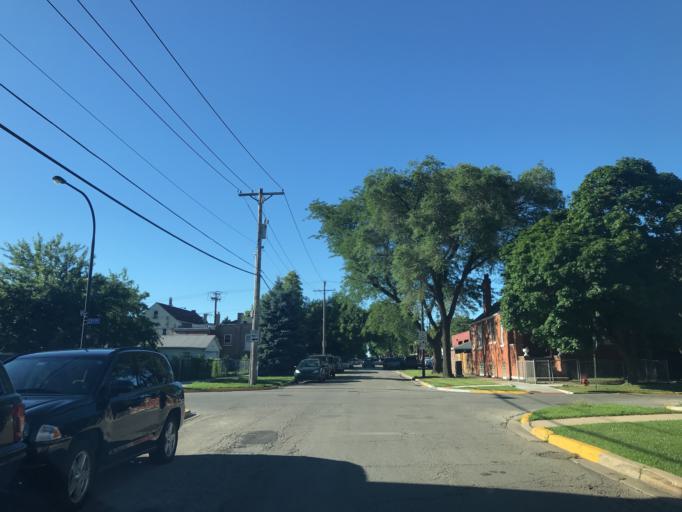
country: US
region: Illinois
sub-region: Cook County
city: Cicero
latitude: 41.8445
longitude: -87.7588
